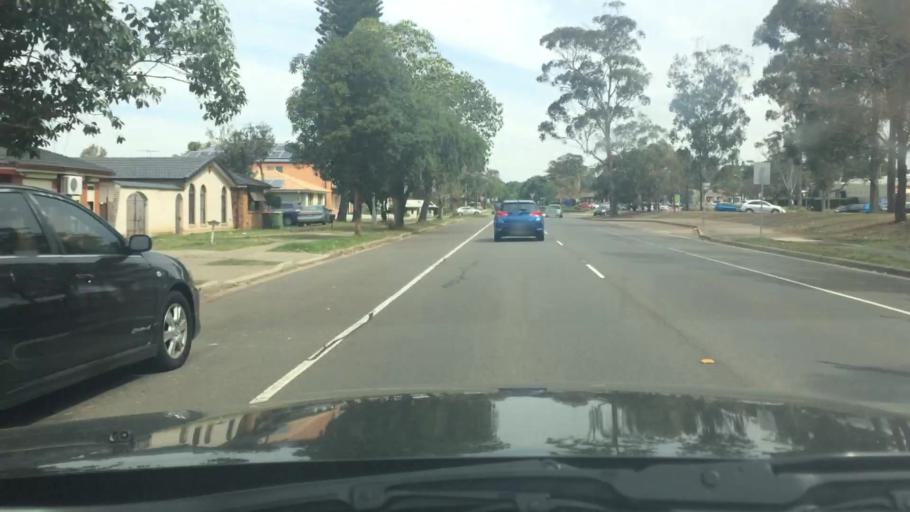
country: AU
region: New South Wales
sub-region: Fairfield
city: Cabramatta West
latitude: -33.8630
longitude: 150.8995
